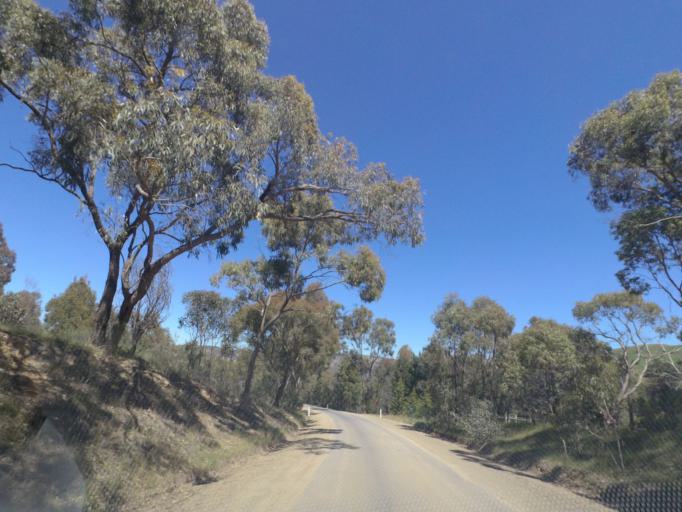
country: AU
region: Victoria
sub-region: Whittlesea
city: Whittlesea
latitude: -37.2845
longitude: 145.0006
